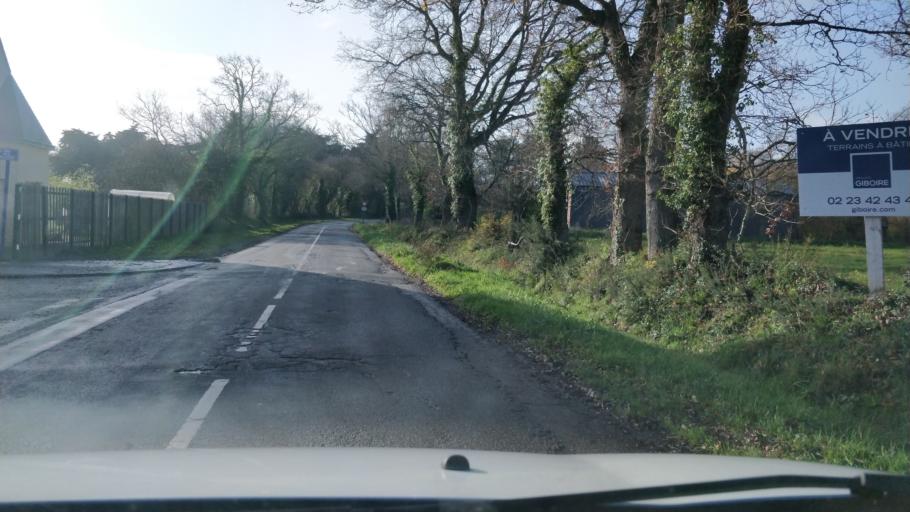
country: FR
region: Pays de la Loire
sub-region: Departement de la Loire-Atlantique
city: Mesquer
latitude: 47.3962
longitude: -2.4641
